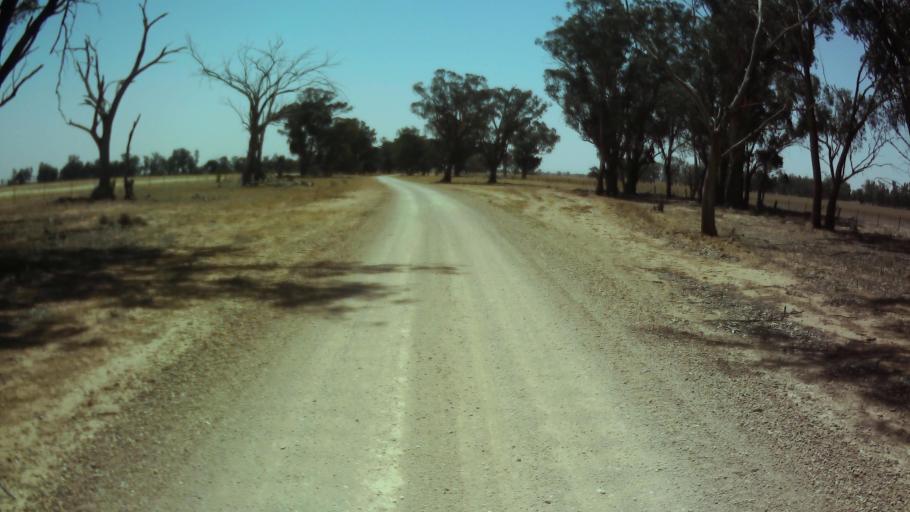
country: AU
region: New South Wales
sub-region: Weddin
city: Grenfell
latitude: -34.0189
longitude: 147.8996
